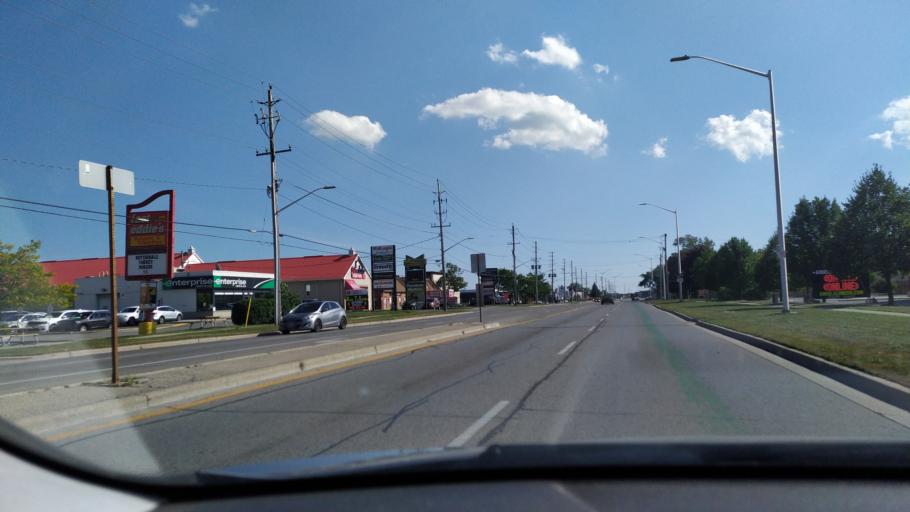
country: CA
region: Ontario
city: London
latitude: 42.9470
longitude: -81.2582
